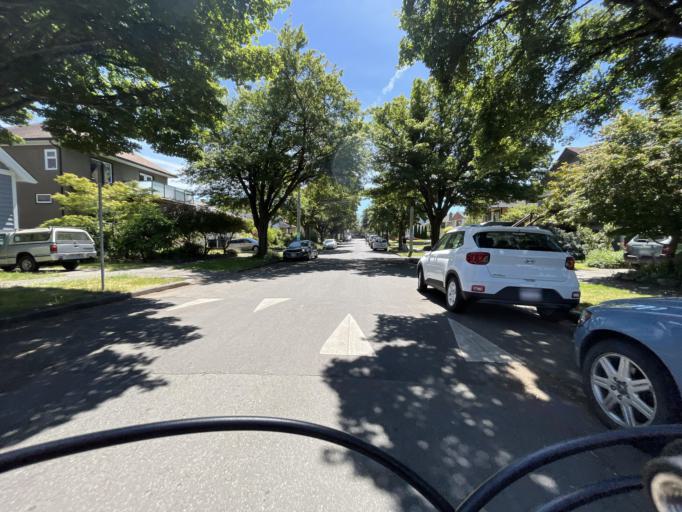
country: CA
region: British Columbia
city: Victoria
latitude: 48.4362
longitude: -123.3549
